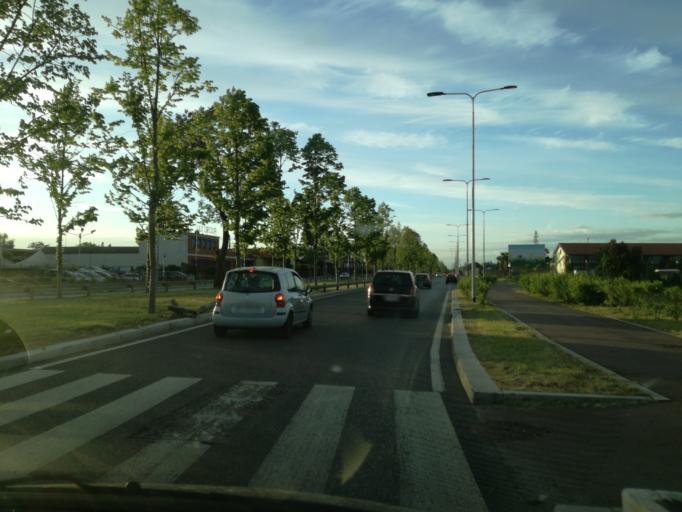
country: IT
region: Lombardy
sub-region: Citta metropolitana di Milano
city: Noverasco-Sporting Mirasole
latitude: 45.4037
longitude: 9.2091
